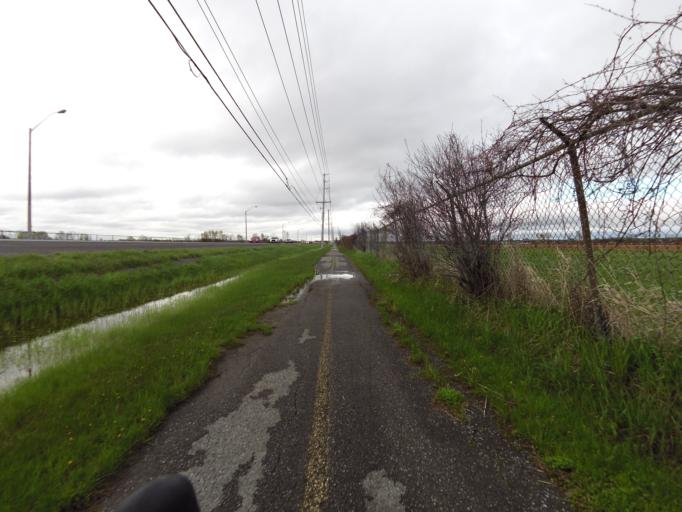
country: CA
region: Ontario
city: Bells Corners
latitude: 45.3041
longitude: -75.7667
